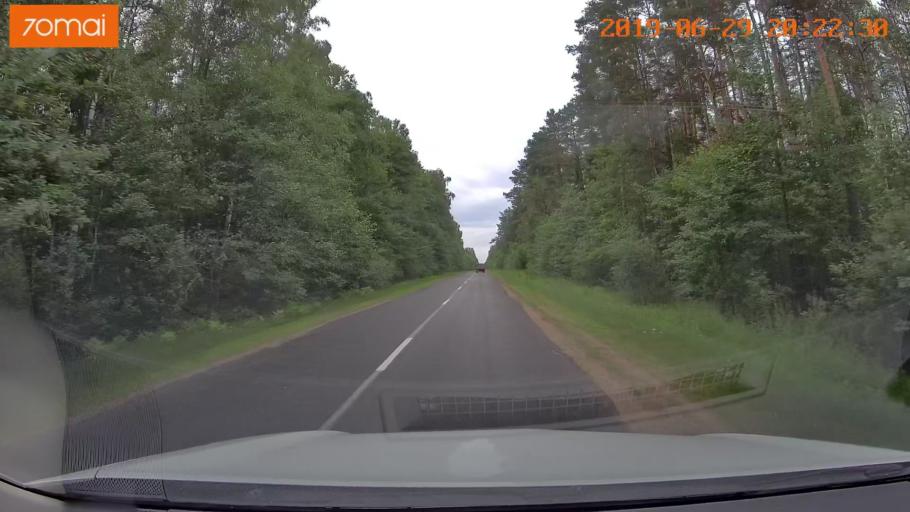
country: BY
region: Brest
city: Asnyezhytsy
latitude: 52.4329
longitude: 26.2551
